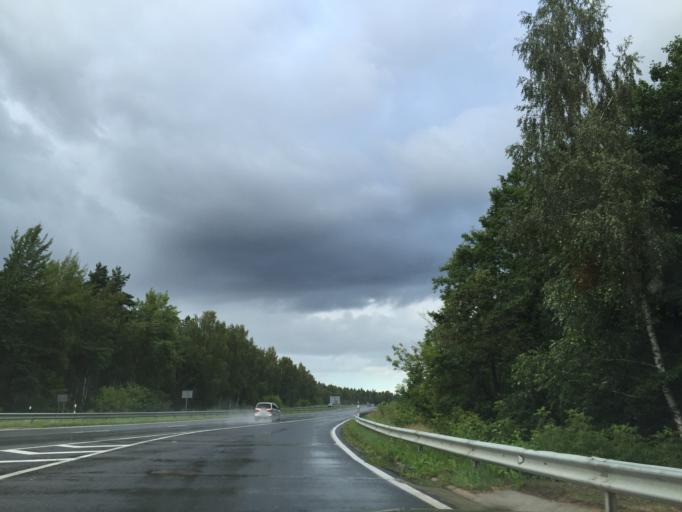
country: LV
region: Babite
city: Pinki
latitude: 56.9571
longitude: 23.9308
